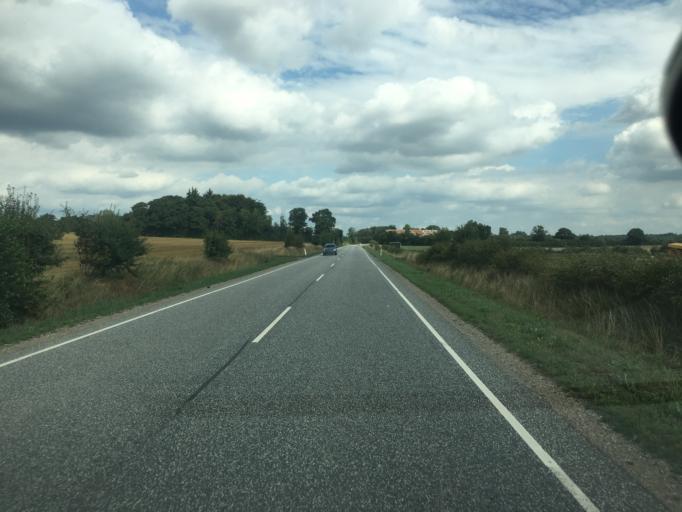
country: DK
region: South Denmark
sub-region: Aabenraa Kommune
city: Rodekro
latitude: 54.9793
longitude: 9.3342
